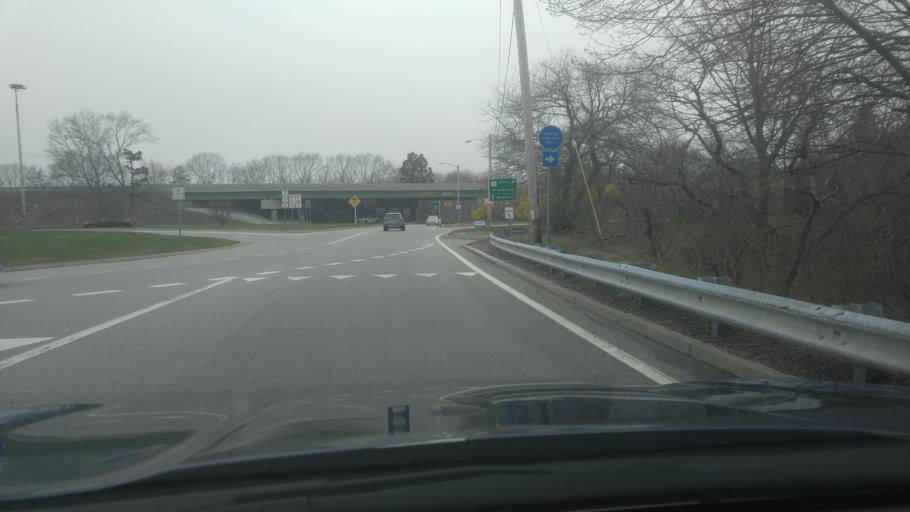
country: US
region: Rhode Island
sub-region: Washington County
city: Wakefield-Peacedale
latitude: 41.4344
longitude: -71.4818
